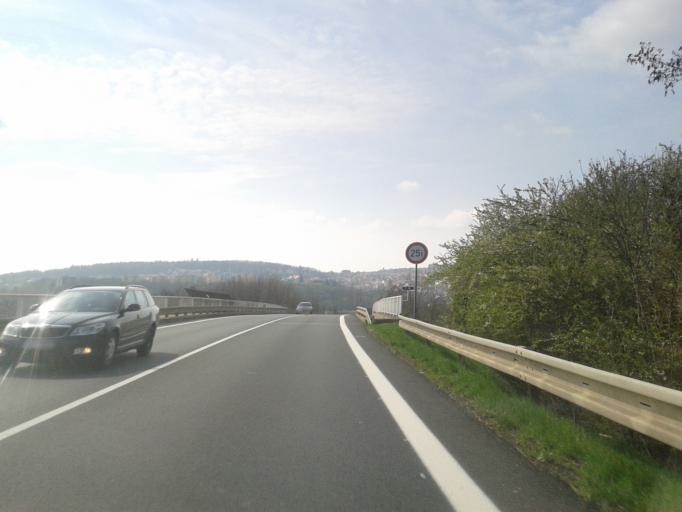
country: CZ
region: Central Bohemia
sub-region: Okres Beroun
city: Horovice
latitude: 49.8493
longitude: 13.9080
